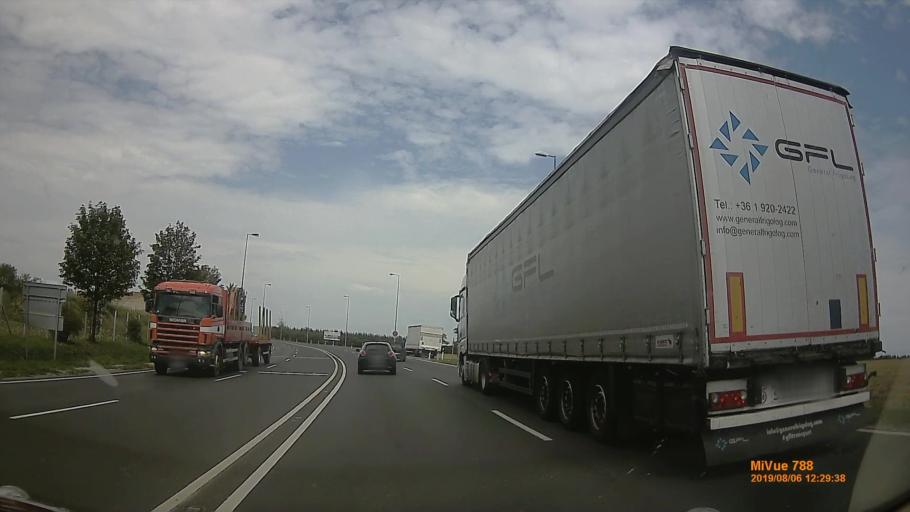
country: HU
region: Vas
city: Szombathely
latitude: 47.2328
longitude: 16.6572
